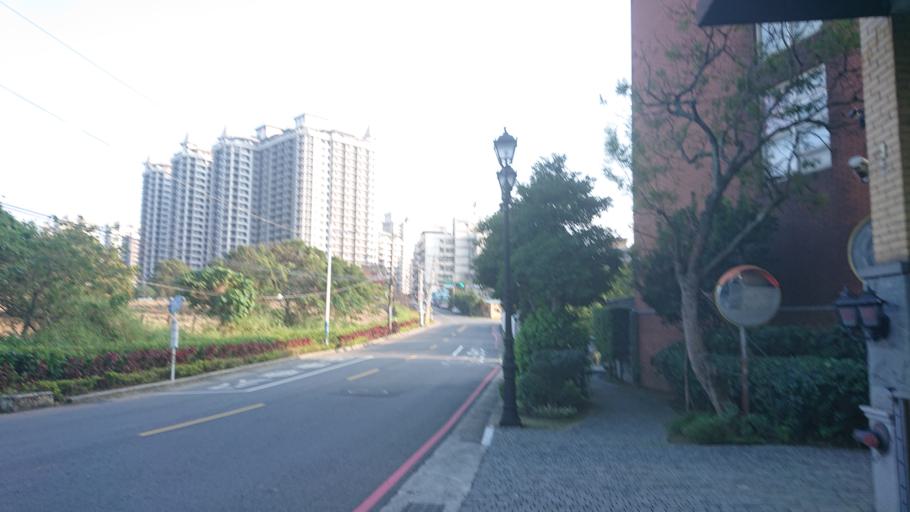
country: TW
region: Taipei
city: Taipei
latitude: 25.1906
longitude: 121.4260
